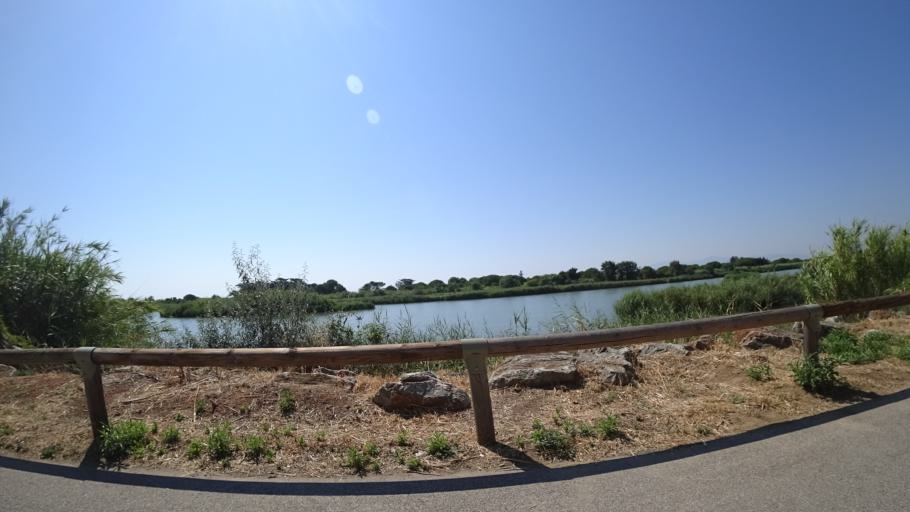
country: FR
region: Languedoc-Roussillon
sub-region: Departement des Pyrenees-Orientales
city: Le Barcares
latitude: 42.7787
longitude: 3.0330
